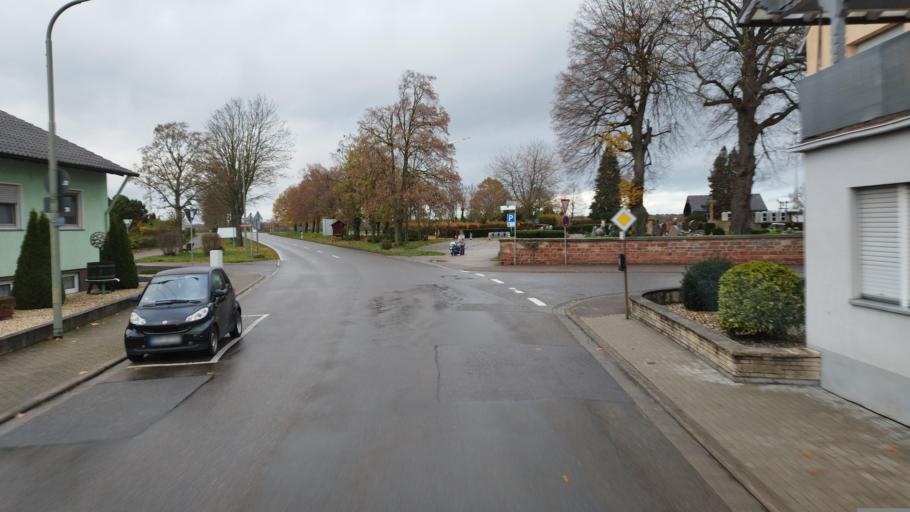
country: DE
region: Rheinland-Pfalz
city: Hatzenbuhl
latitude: 49.1146
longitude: 8.2423
